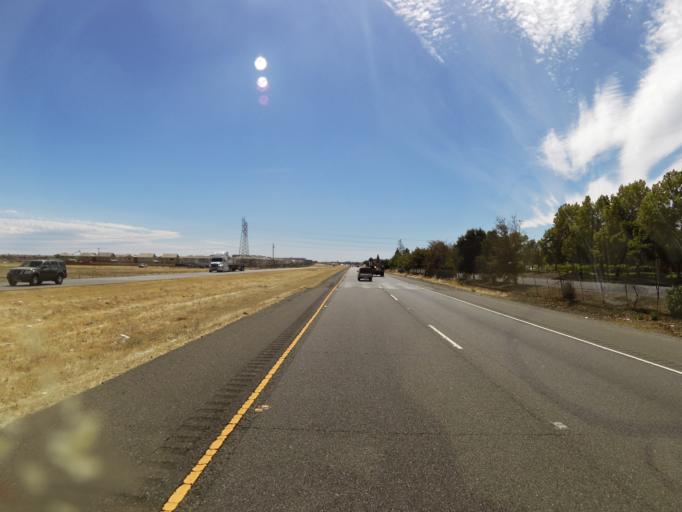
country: US
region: California
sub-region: Solano County
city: Hartley
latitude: 38.4055
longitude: -121.9473
